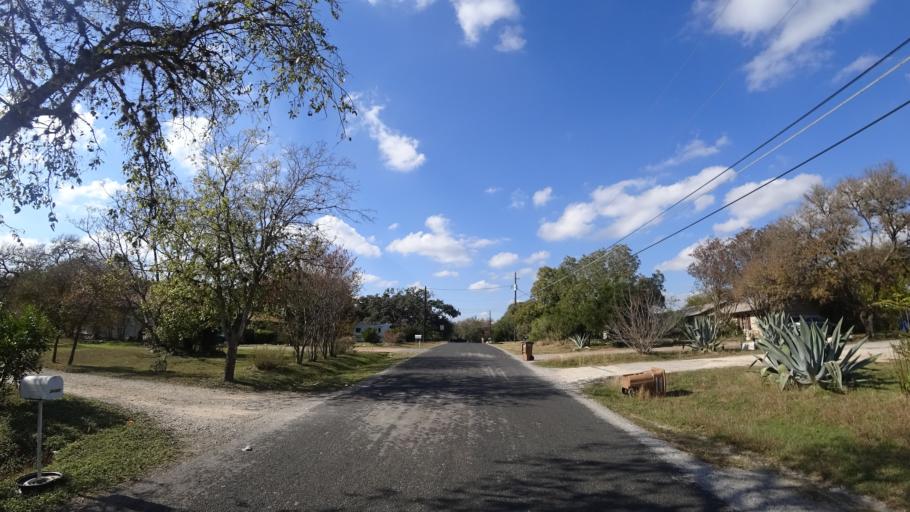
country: US
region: Texas
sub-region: Travis County
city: Shady Hollow
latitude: 30.1819
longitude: -97.8494
